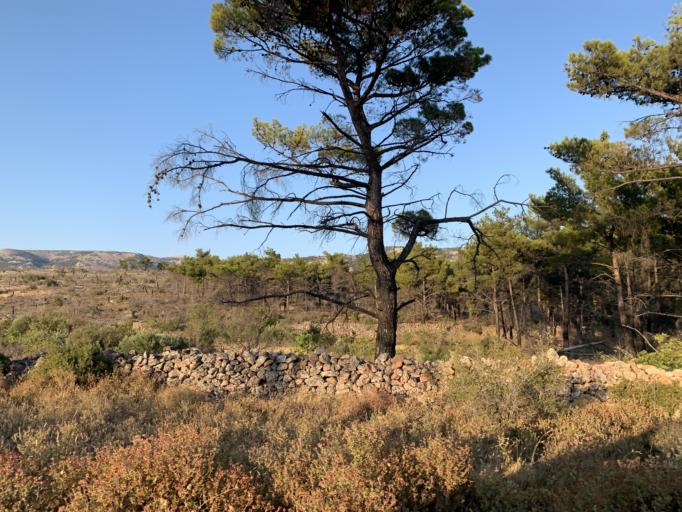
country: GR
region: North Aegean
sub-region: Chios
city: Vrontados
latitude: 38.3818
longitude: 26.0182
